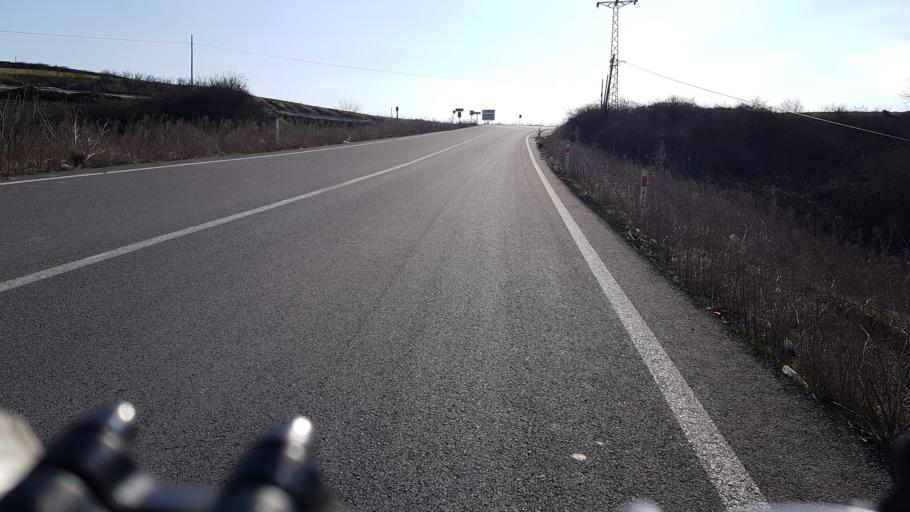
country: TR
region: Tekirdag
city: Velimese
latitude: 41.3559
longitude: 27.8492
